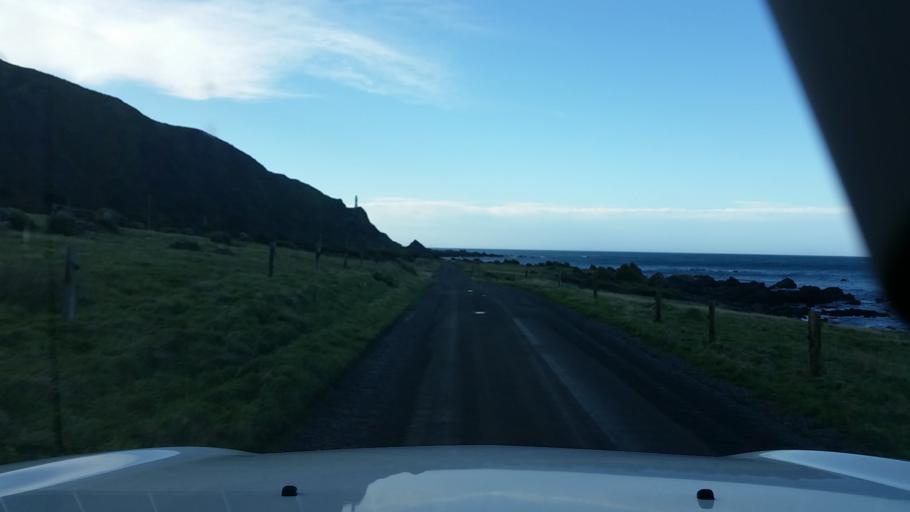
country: NZ
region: Wellington
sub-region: South Wairarapa District
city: Waipawa
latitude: -41.6104
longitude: 175.2774
